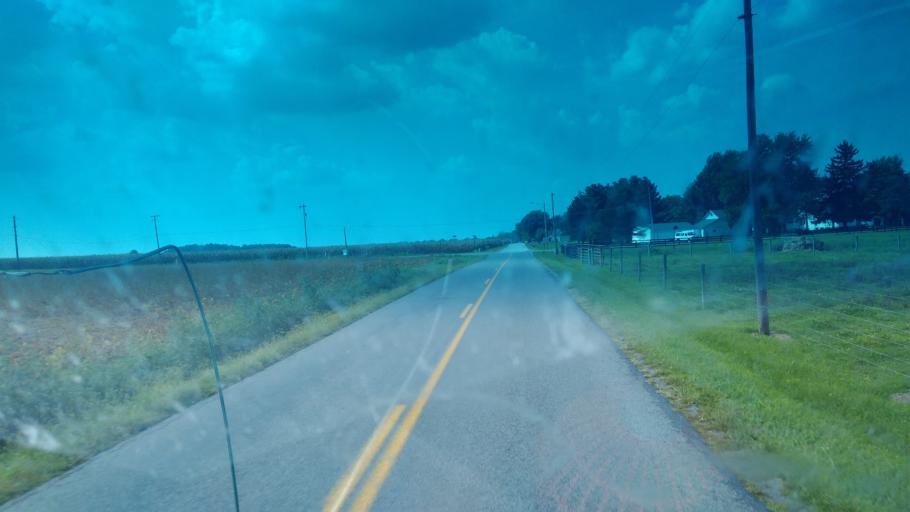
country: US
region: Ohio
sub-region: Hardin County
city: Ada
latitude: 40.7029
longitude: -83.9169
